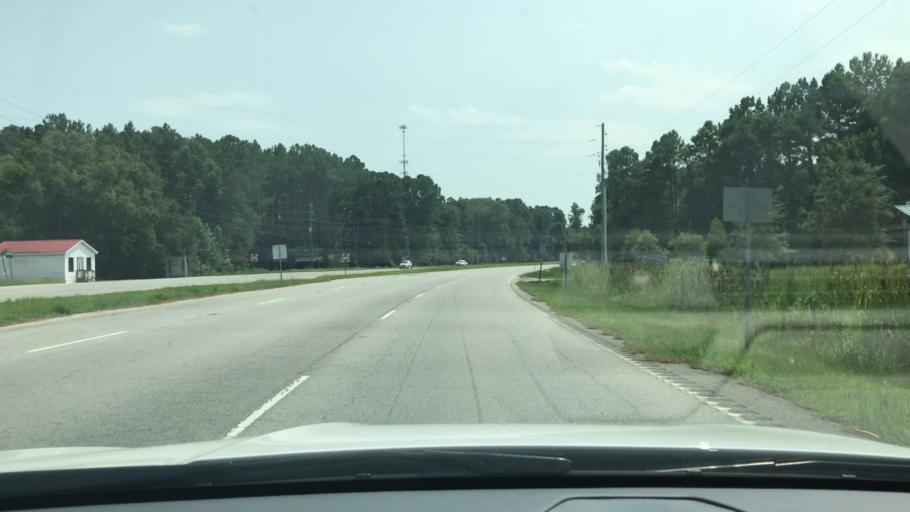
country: US
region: South Carolina
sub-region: Charleston County
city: Awendaw
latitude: 32.9912
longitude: -79.6460
